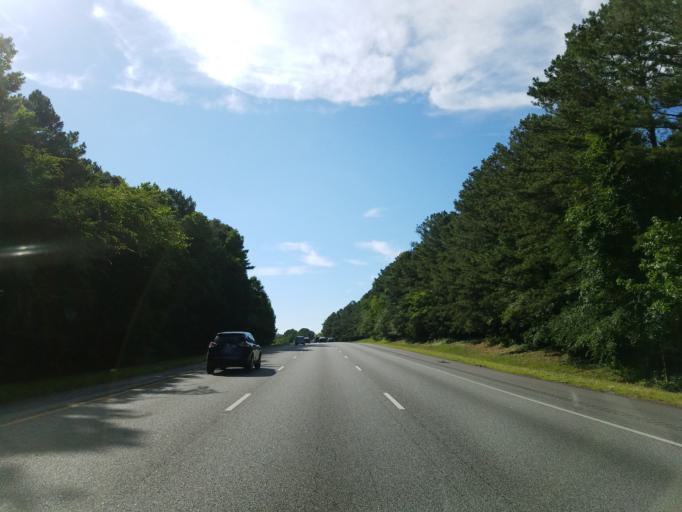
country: US
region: Georgia
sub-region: Bartow County
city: Cartersville
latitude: 34.2514
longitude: -84.7848
